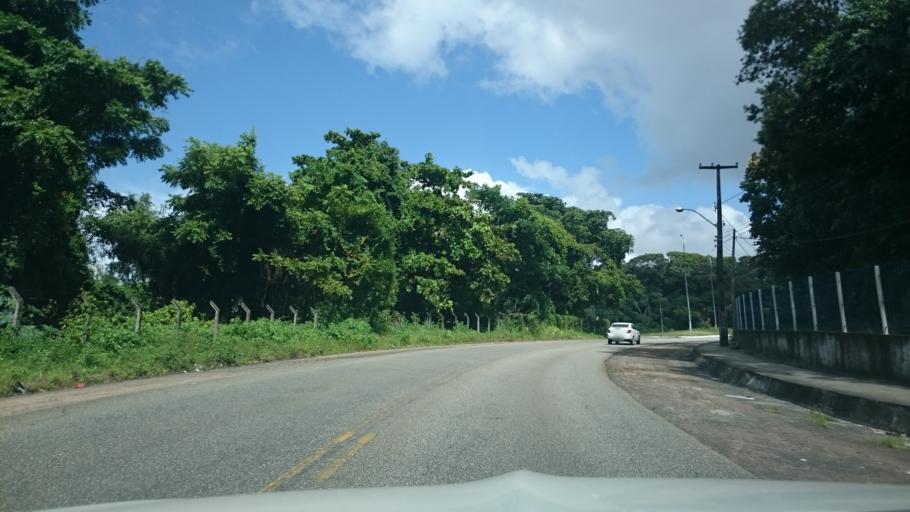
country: BR
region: Paraiba
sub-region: Joao Pessoa
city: Joao Pessoa
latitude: -7.1447
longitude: -34.8494
